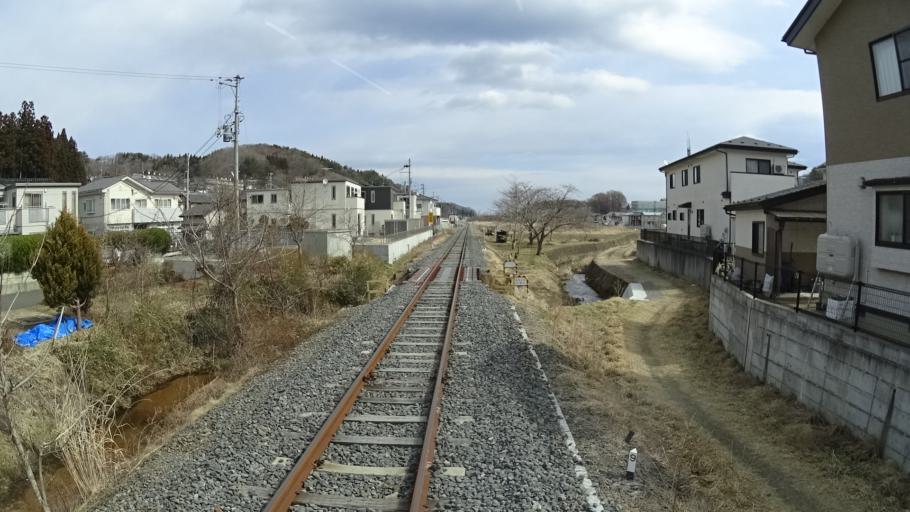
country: JP
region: Iwate
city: Miyako
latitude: 39.6180
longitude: 141.9444
